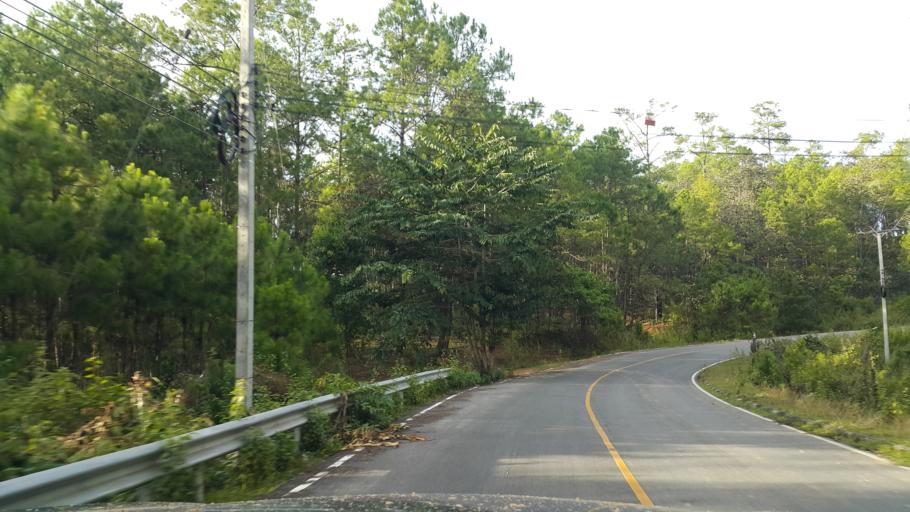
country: TH
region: Chiang Mai
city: Chaem Luang
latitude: 19.0869
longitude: 98.3385
